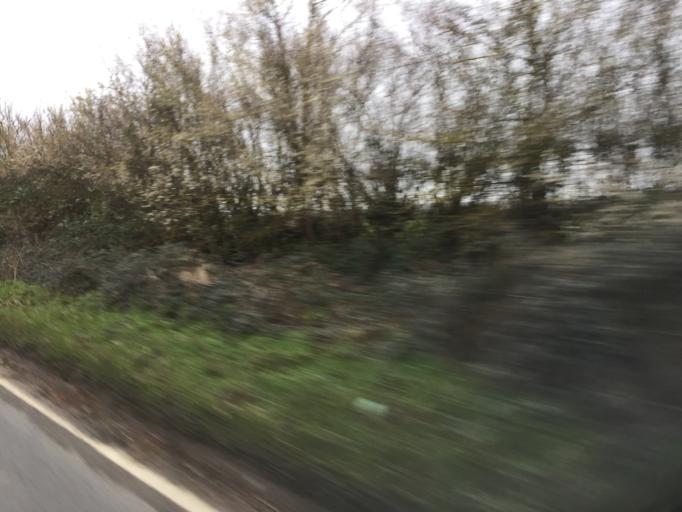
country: GB
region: England
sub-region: Oxfordshire
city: Stanford in the Vale
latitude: 51.6076
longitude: -1.4781
